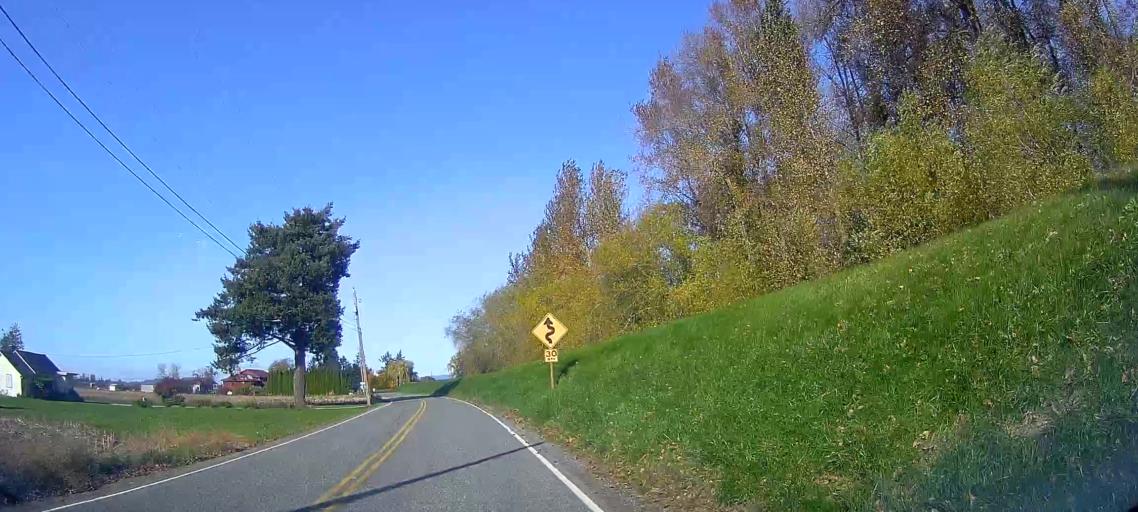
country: US
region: Washington
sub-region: Skagit County
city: Mount Vernon
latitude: 48.4071
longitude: -122.3677
